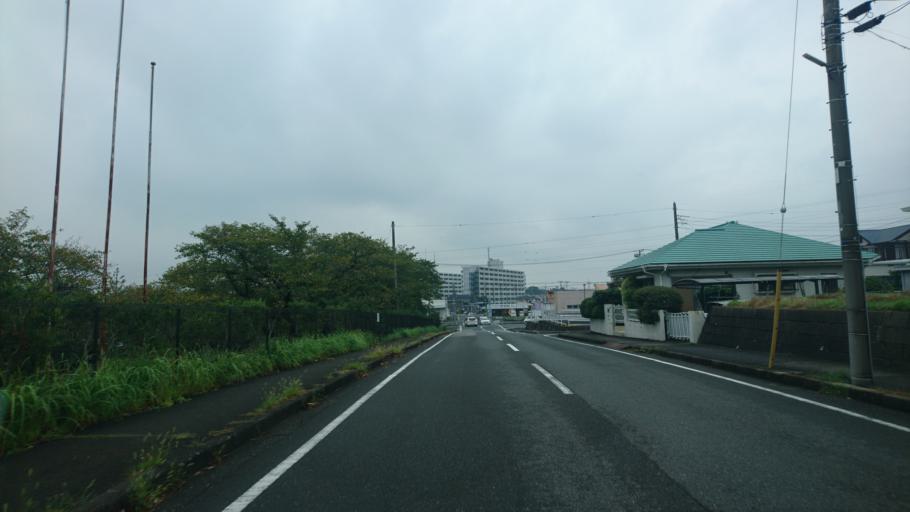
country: JP
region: Chiba
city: Kimitsu
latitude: 35.3260
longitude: 139.9266
